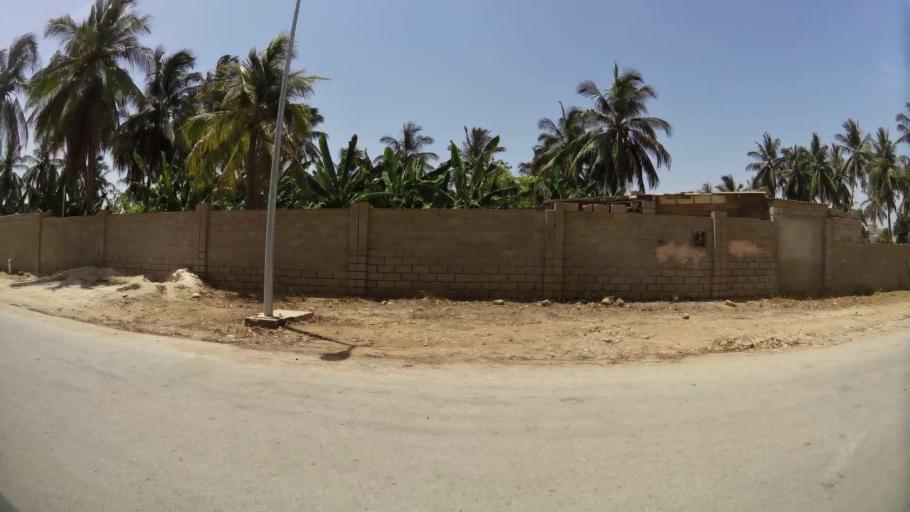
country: OM
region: Zufar
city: Salalah
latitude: 17.0553
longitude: 54.1524
